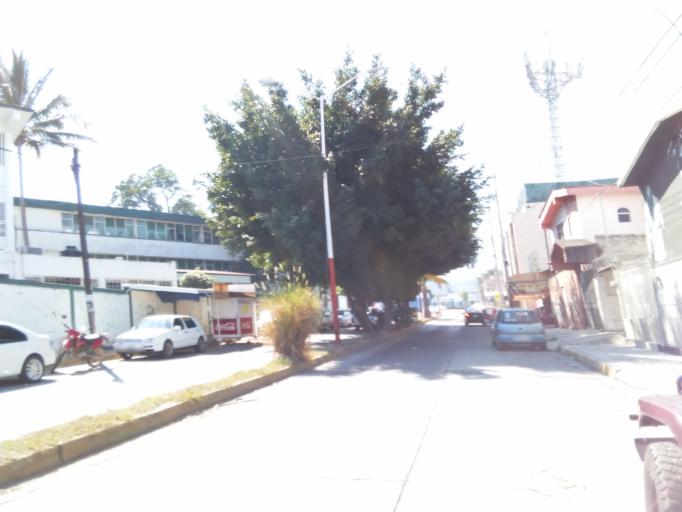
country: MX
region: Nayarit
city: Tepic
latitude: 21.4951
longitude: -104.8943
